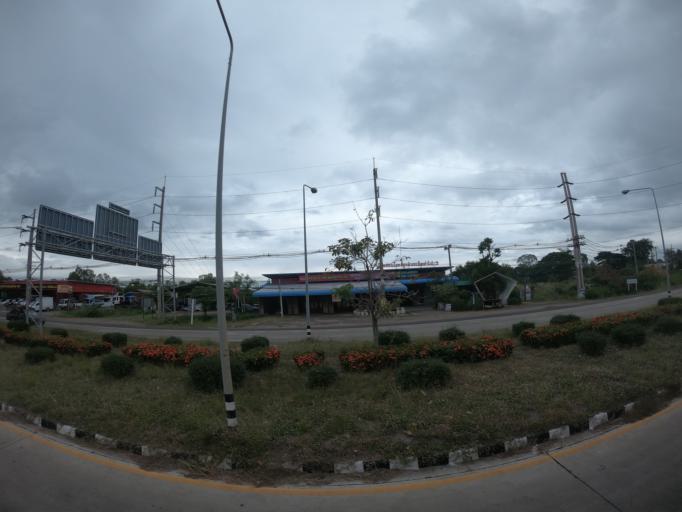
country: TH
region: Roi Et
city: Roi Et
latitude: 16.0430
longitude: 103.6317
